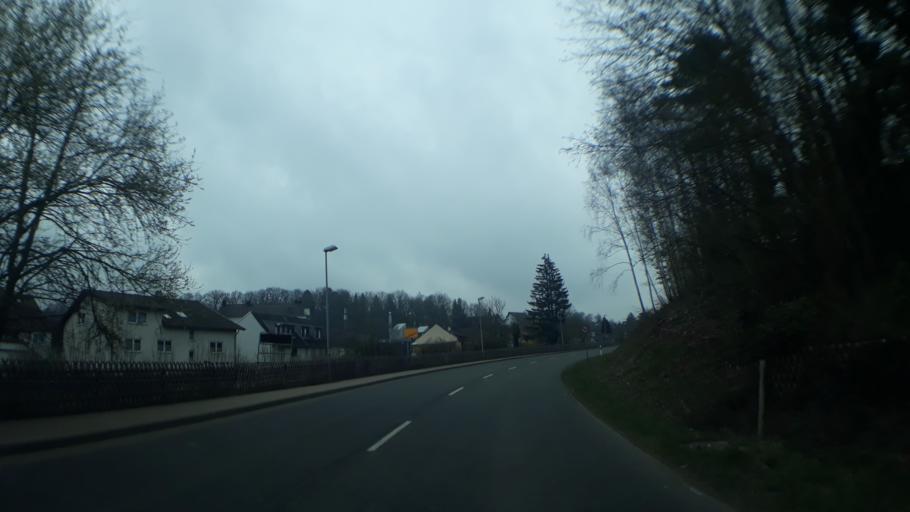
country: DE
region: North Rhine-Westphalia
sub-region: Regierungsbezirk Koln
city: Kall
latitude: 50.5398
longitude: 6.5587
